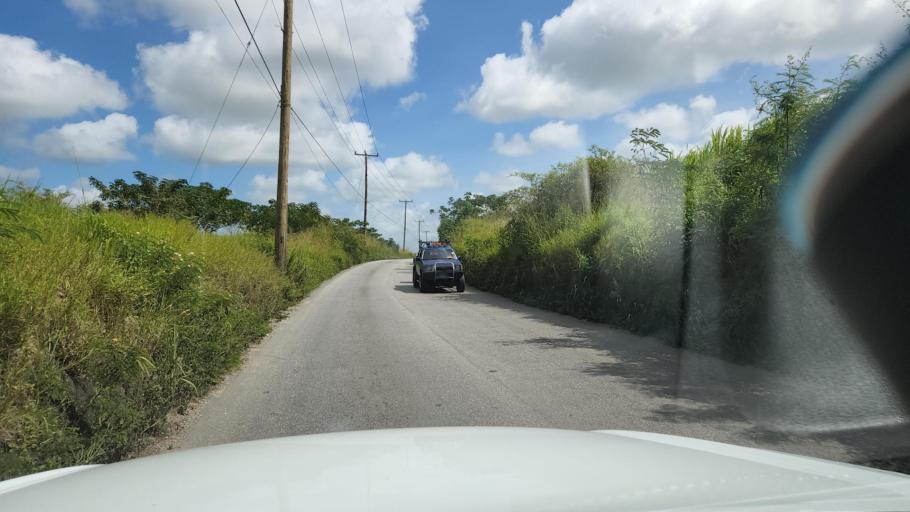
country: BB
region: Christ Church
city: Oistins
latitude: 13.1077
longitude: -59.5591
